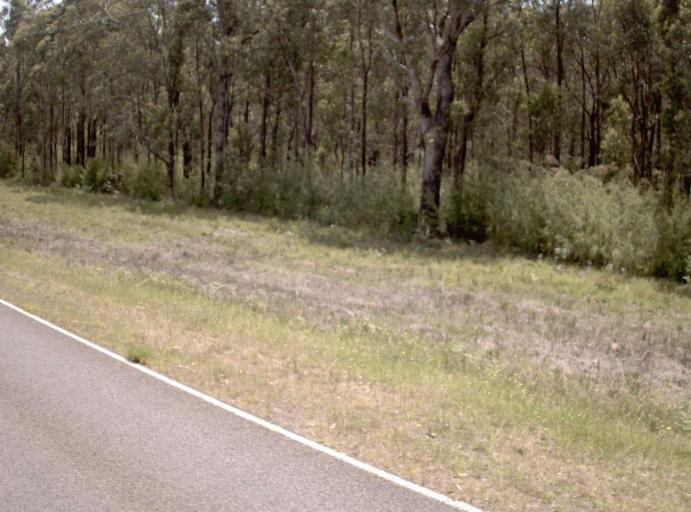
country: AU
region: Victoria
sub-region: Latrobe
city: Moe
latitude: -38.0738
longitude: 146.3308
